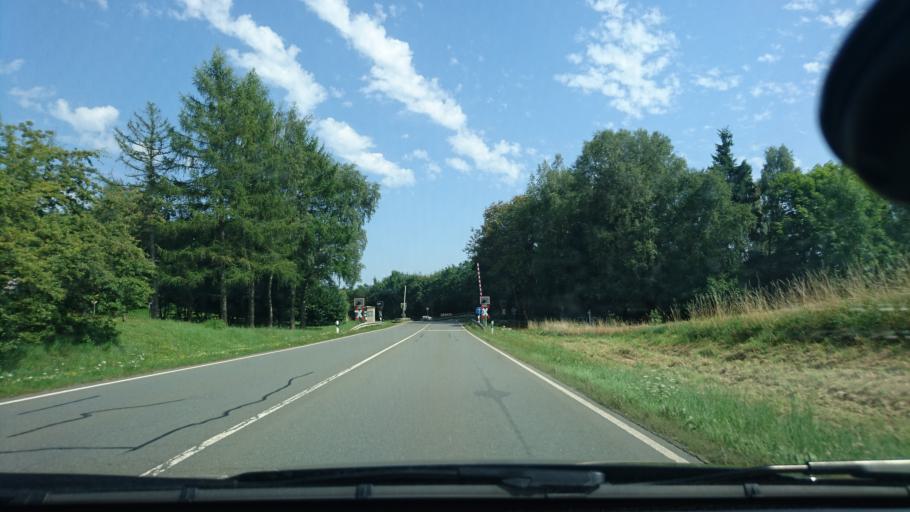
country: DE
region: Bavaria
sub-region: Upper Franconia
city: Selbitz
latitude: 50.3167
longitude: 11.7394
